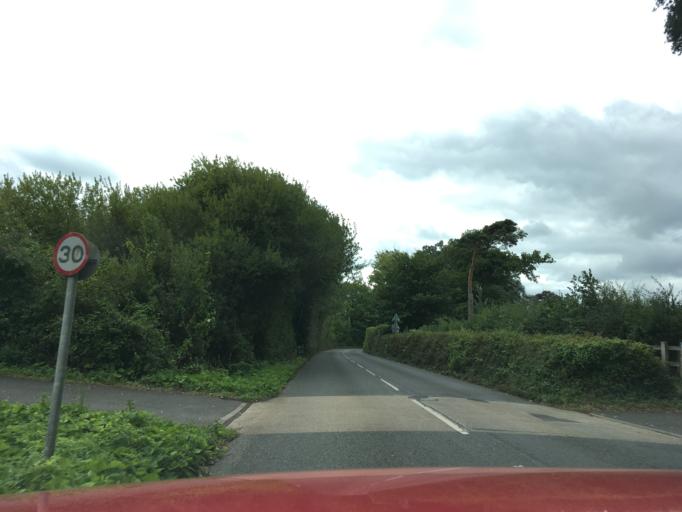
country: GB
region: England
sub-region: Devon
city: Starcross
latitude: 50.6068
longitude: -3.4459
